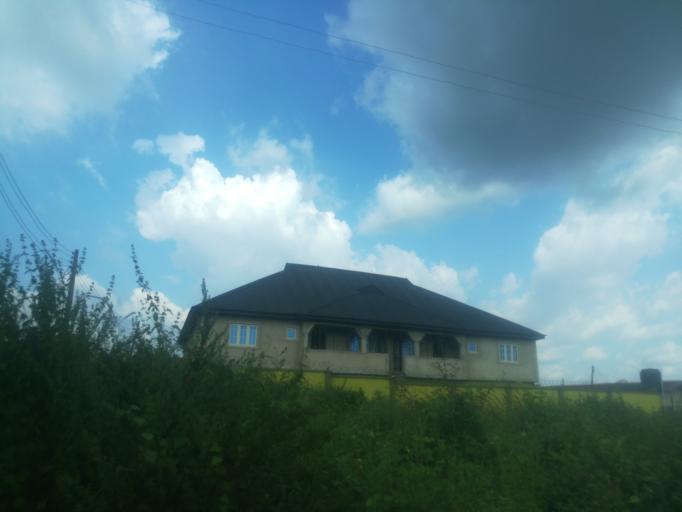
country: NG
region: Oyo
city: Ibadan
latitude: 7.3966
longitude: 3.8367
